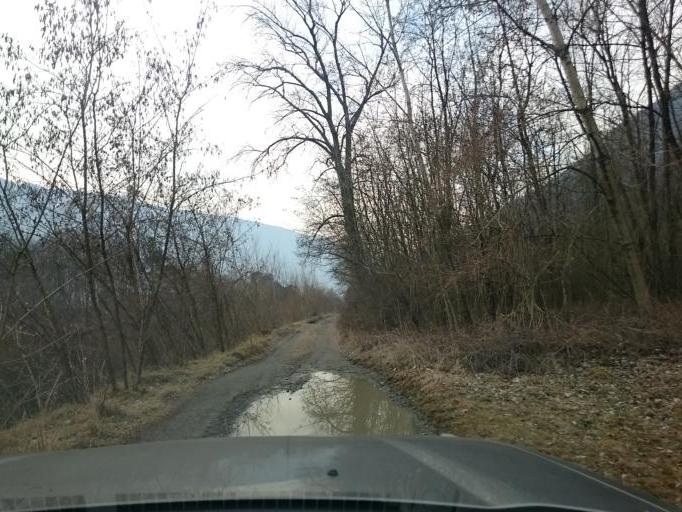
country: IT
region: Lombardy
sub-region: Provincia di Sondrio
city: Mazzo di Valtellina
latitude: 46.2581
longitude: 10.2487
